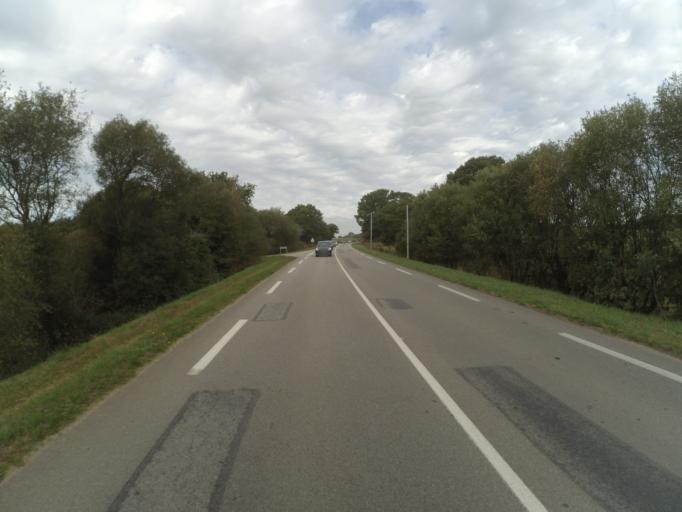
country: FR
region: Brittany
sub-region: Departement du Morbihan
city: Merlevenez
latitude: 47.7189
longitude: -3.2289
